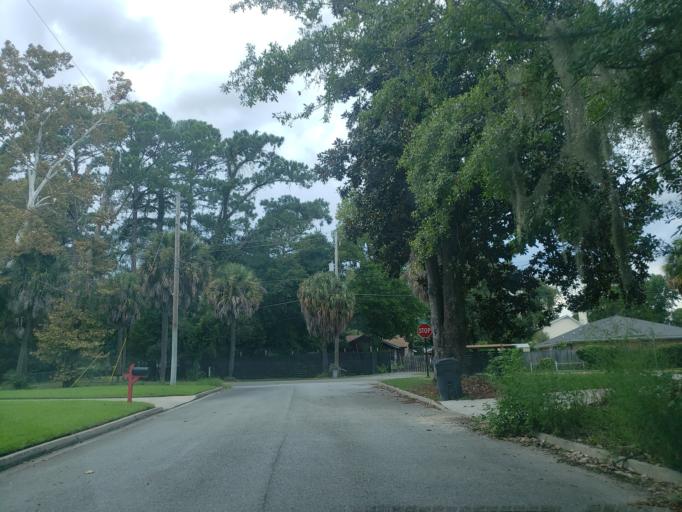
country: US
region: Georgia
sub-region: Chatham County
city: Isle of Hope
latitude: 31.9881
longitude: -81.0709
